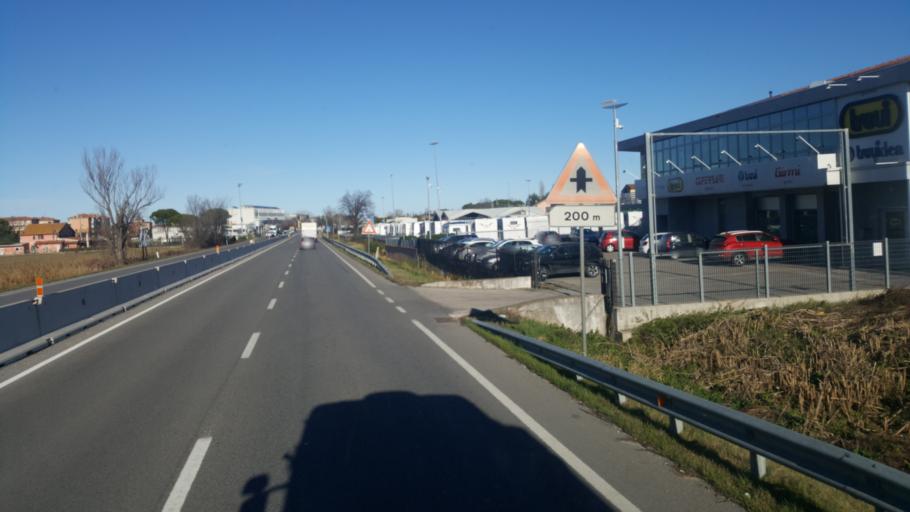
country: IT
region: Emilia-Romagna
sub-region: Provincia di Rimini
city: Rimini
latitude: 44.0290
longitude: 12.5541
